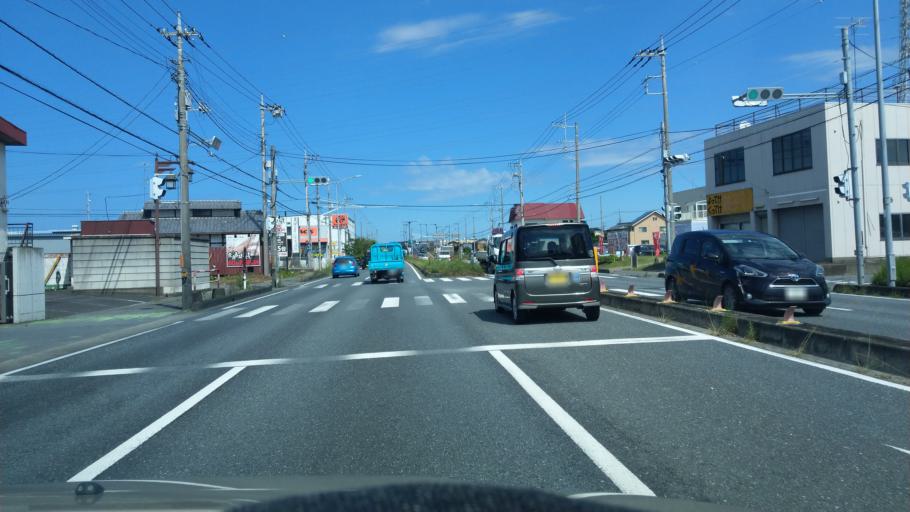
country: JP
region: Saitama
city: Sakado
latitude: 36.0199
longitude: 139.4248
